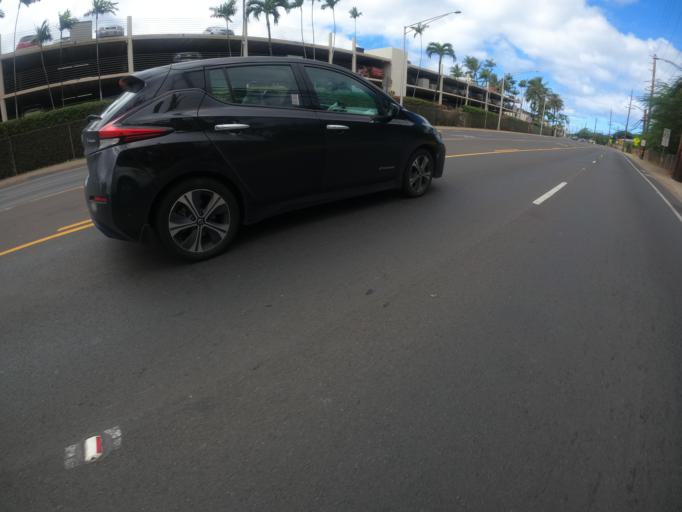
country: US
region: Hawaii
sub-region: Honolulu County
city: Makaha
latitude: 21.4579
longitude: -158.2021
